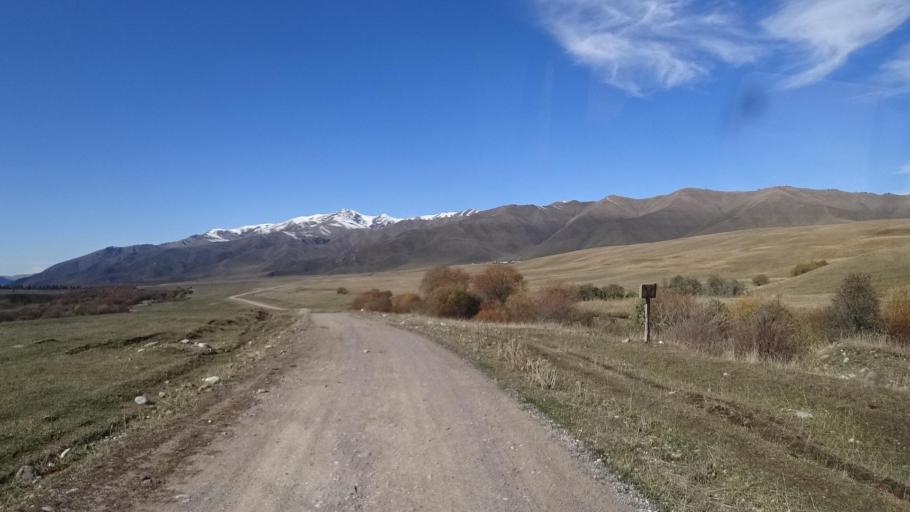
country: KZ
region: Almaty Oblysy
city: Kegen
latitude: 42.7359
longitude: 79.0170
